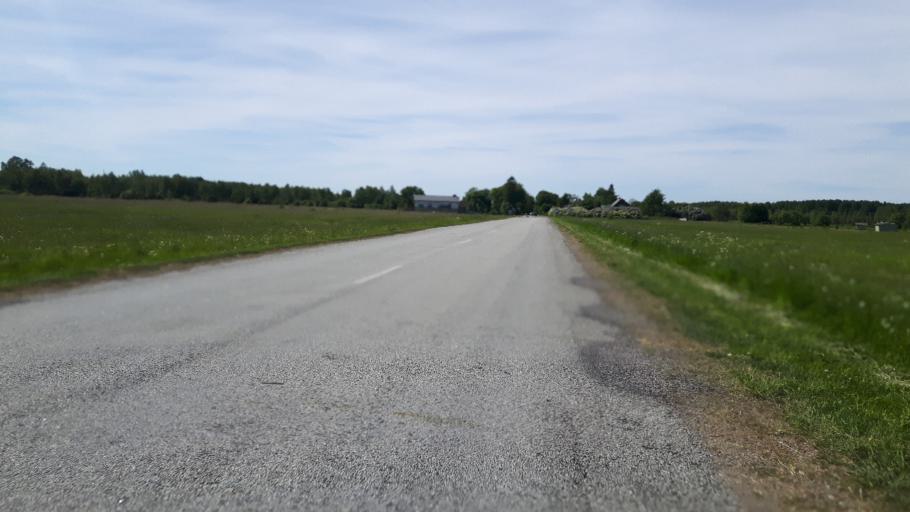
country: EE
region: Harju
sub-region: Kuusalu vald
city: Kuusalu
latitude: 59.4665
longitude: 25.3192
